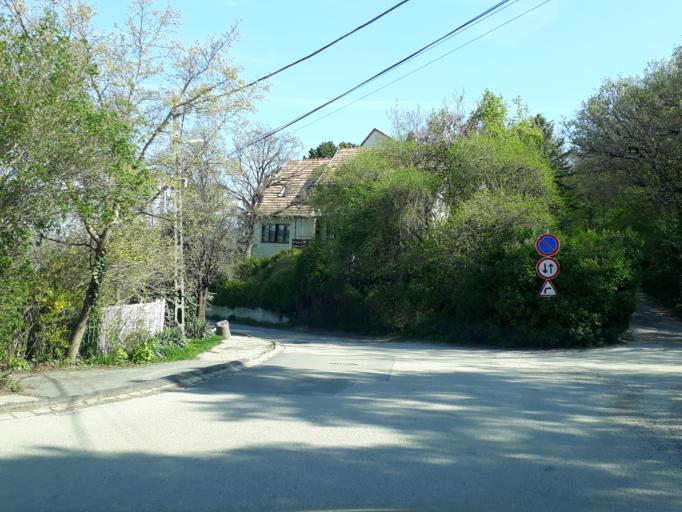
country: HU
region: Pest
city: Budakeszi
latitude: 47.5072
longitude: 18.9338
